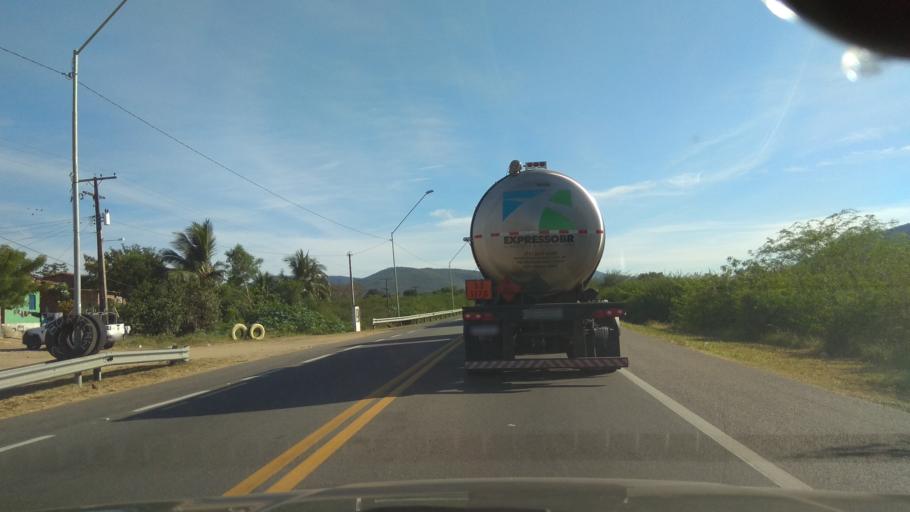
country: BR
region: Bahia
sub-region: Jequie
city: Jequie
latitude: -13.8263
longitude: -40.1108
